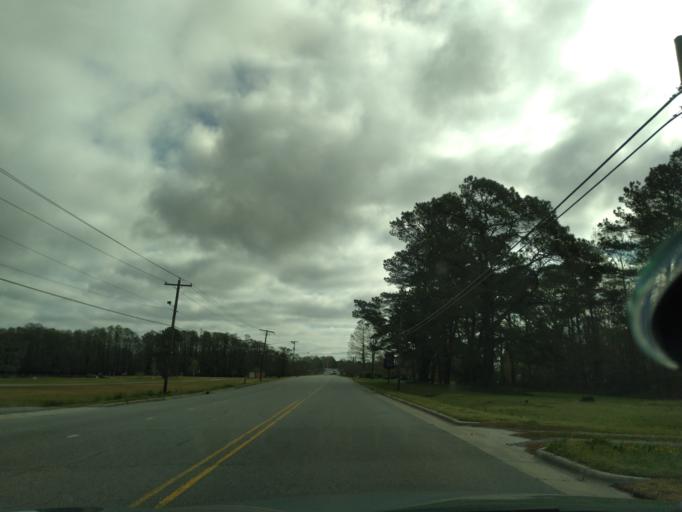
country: US
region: North Carolina
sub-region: Chowan County
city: Edenton
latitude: 36.0570
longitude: -76.6295
